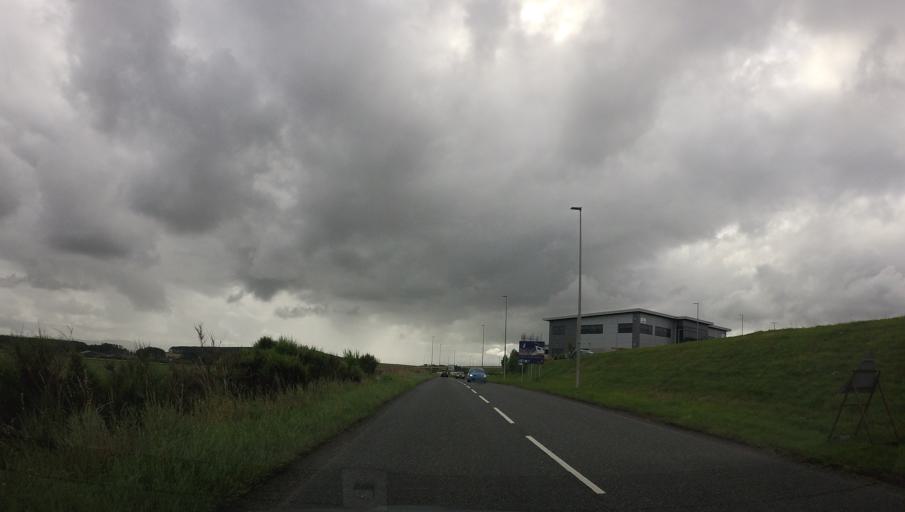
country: GB
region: Scotland
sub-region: Aberdeenshire
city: Westhill
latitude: 57.1460
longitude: -2.2700
